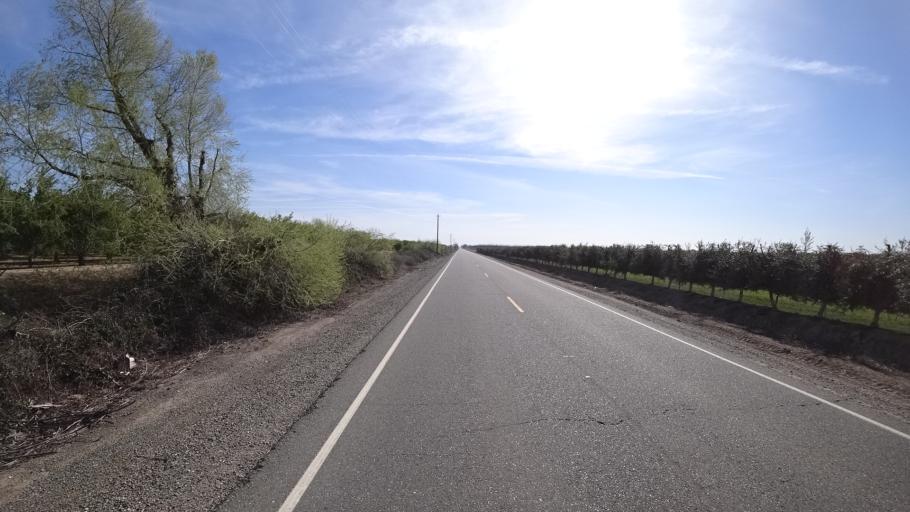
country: US
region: California
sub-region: Glenn County
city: Willows
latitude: 39.6245
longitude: -122.2268
